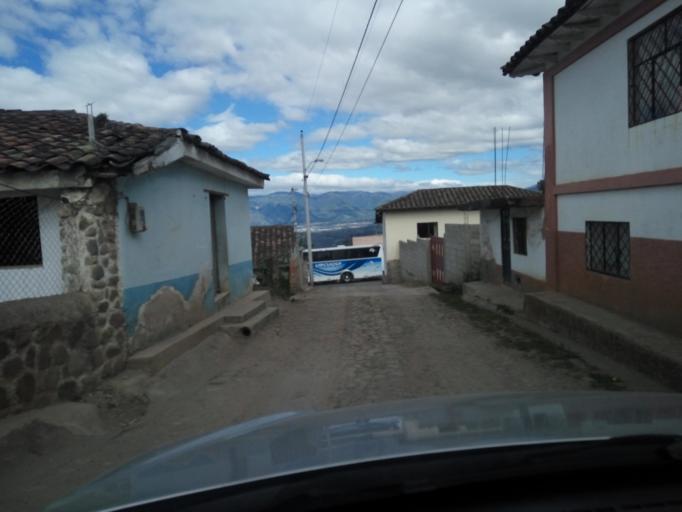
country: EC
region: Imbabura
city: Atuntaqui
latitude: 0.4047
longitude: -78.2484
